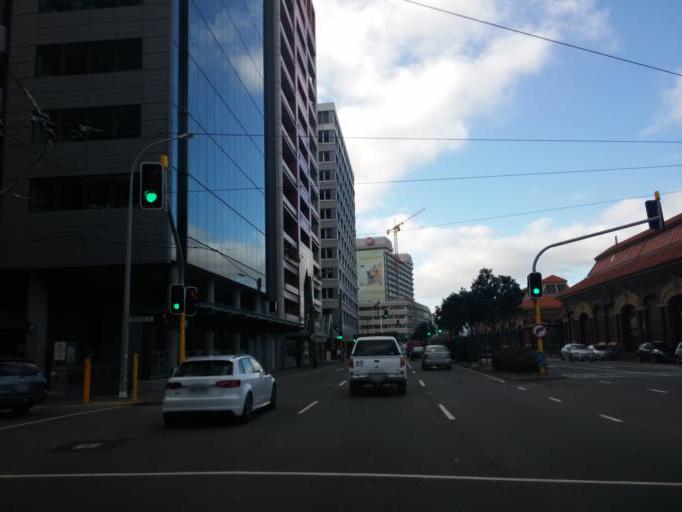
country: NZ
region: Wellington
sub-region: Wellington City
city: Wellington
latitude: -41.2839
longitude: 174.7777
